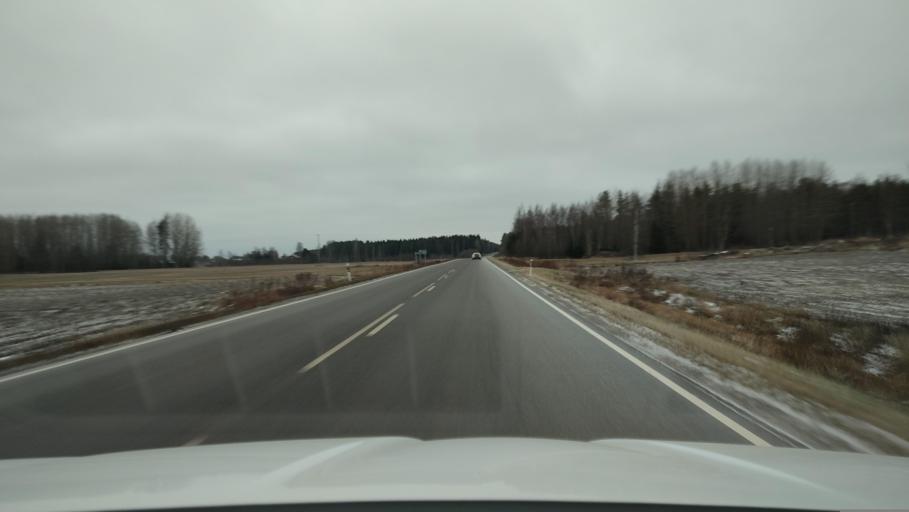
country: FI
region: Ostrobothnia
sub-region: Sydosterbotten
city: Naerpes
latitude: 62.5442
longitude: 21.4687
